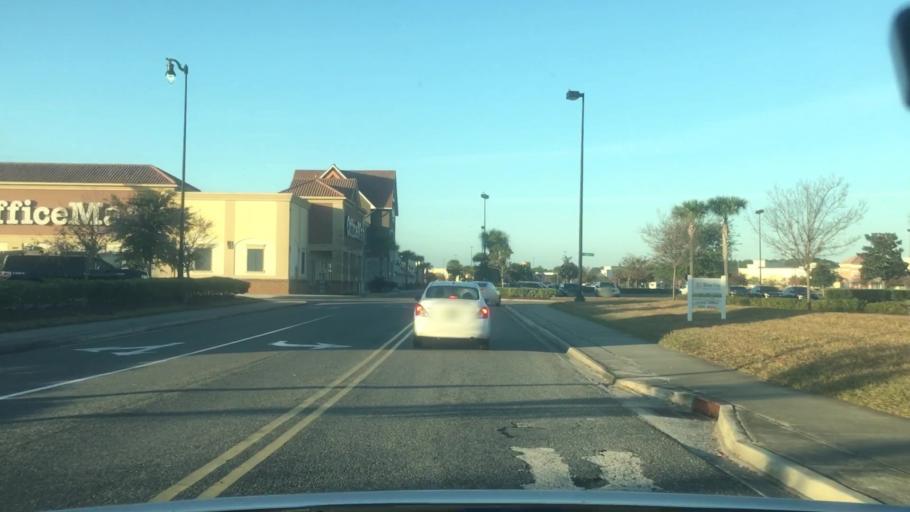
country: US
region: Florida
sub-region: Duval County
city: Jacksonville
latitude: 30.4796
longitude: -81.6366
